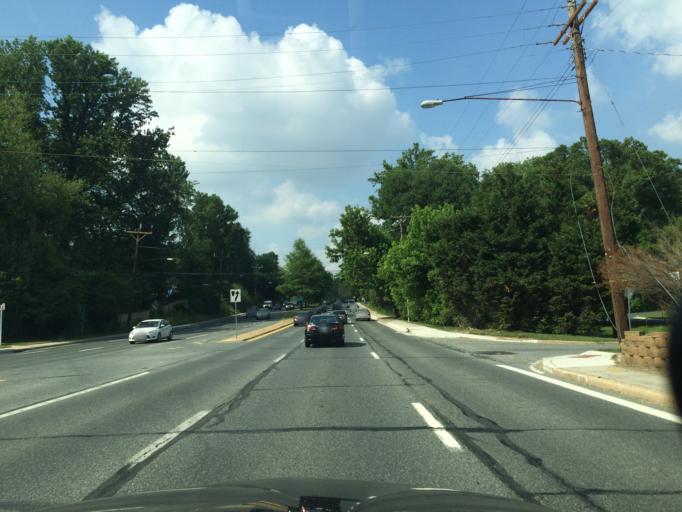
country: US
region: Maryland
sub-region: Montgomery County
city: South Kensington
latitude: 39.0124
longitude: -77.0804
